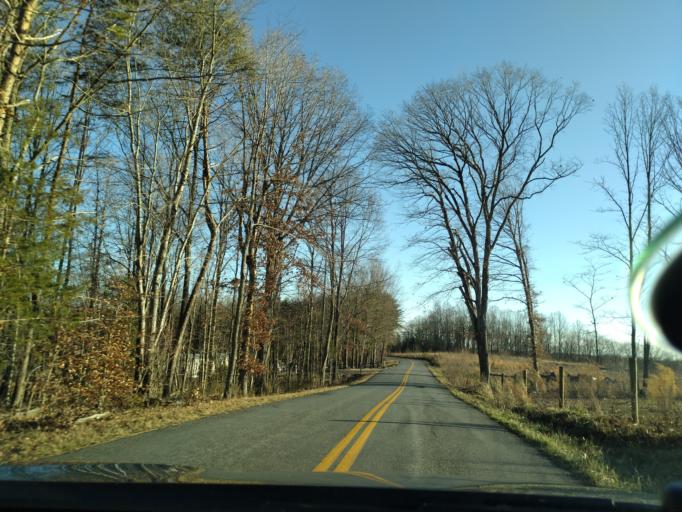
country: US
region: Virginia
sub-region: Prince Edward County
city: Hampden Sydney
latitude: 37.3243
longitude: -78.5766
